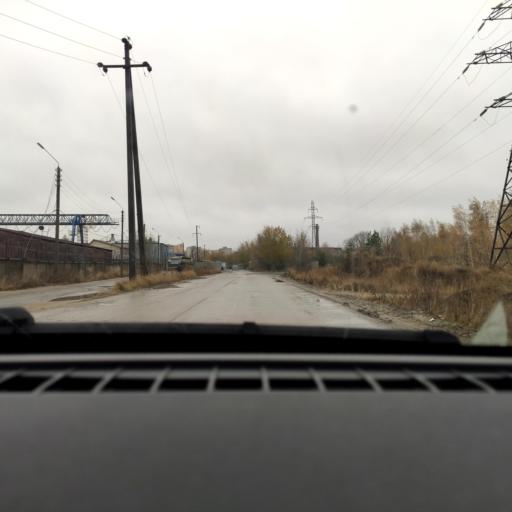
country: RU
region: Voronezj
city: Maslovka
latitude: 51.5916
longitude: 39.2531
